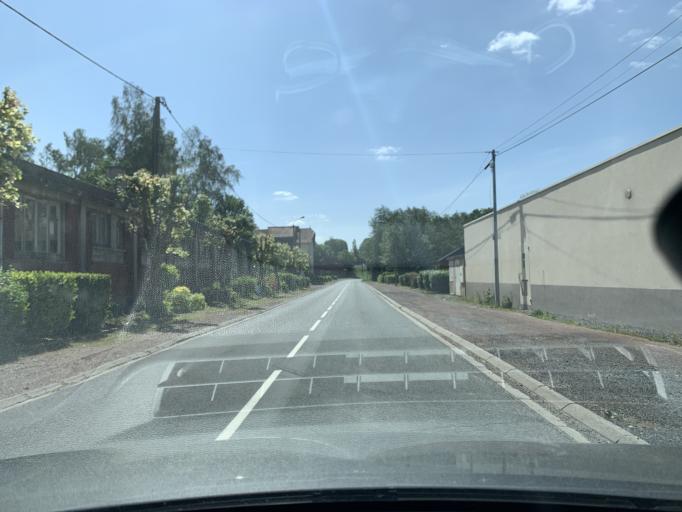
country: FR
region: Nord-Pas-de-Calais
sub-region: Departement du Nord
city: Marcoing
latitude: 50.1275
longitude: 3.1903
